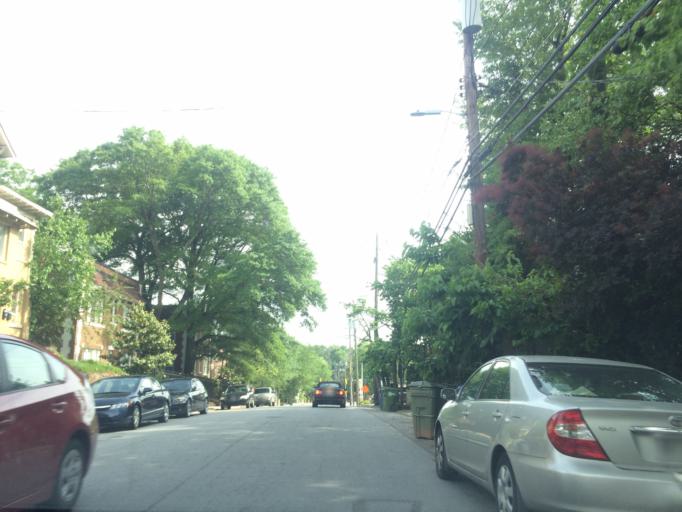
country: US
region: Georgia
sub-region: DeKalb County
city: Druid Hills
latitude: 33.7752
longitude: -84.3587
